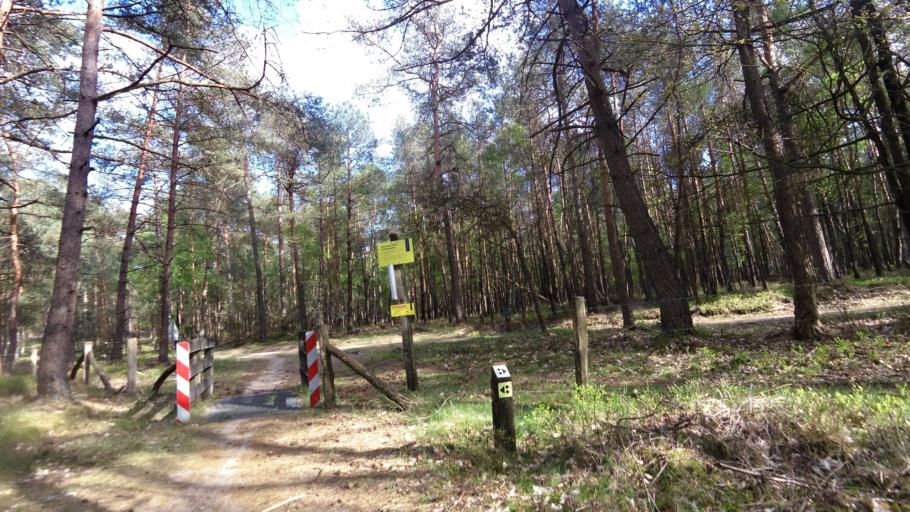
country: NL
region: Gelderland
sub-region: Gemeente Apeldoorn
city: Loenen
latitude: 52.0779
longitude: 5.9737
